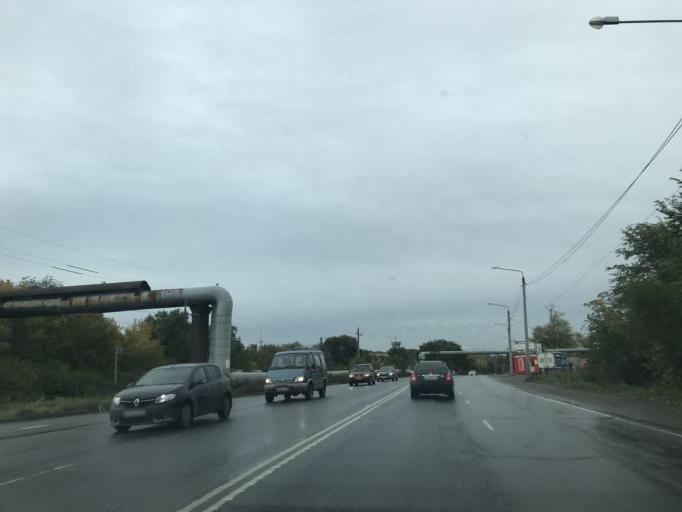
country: RU
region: Chelyabinsk
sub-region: Gorod Chelyabinsk
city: Chelyabinsk
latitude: 55.1988
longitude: 61.4076
